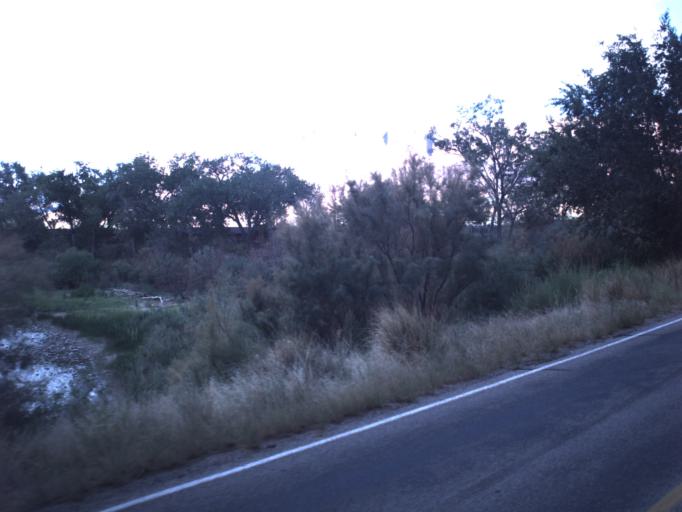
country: US
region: Utah
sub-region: Grand County
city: Moab
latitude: 38.6819
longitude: -109.4556
